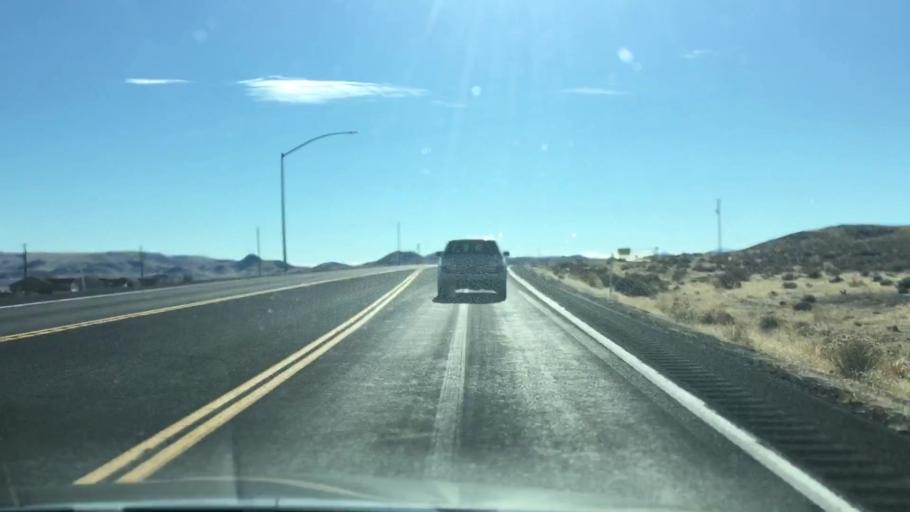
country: US
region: Nevada
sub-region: Lyon County
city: Silver Springs
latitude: 39.3334
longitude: -119.2414
